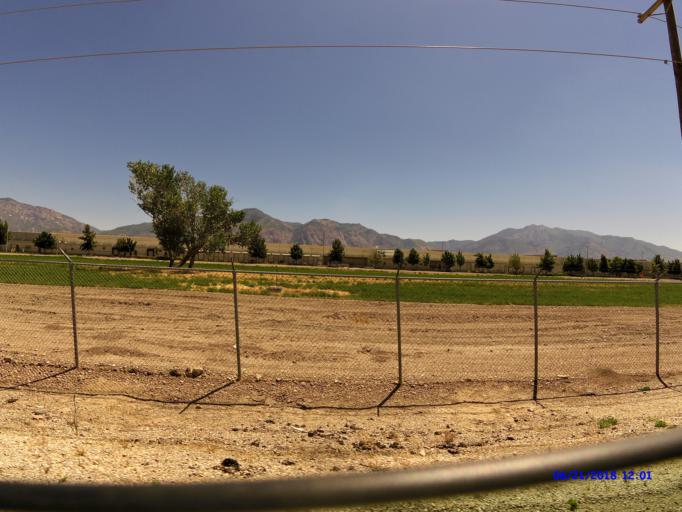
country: US
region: Utah
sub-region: Weber County
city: Marriott-Slaterville
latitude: 41.2651
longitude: -112.0089
